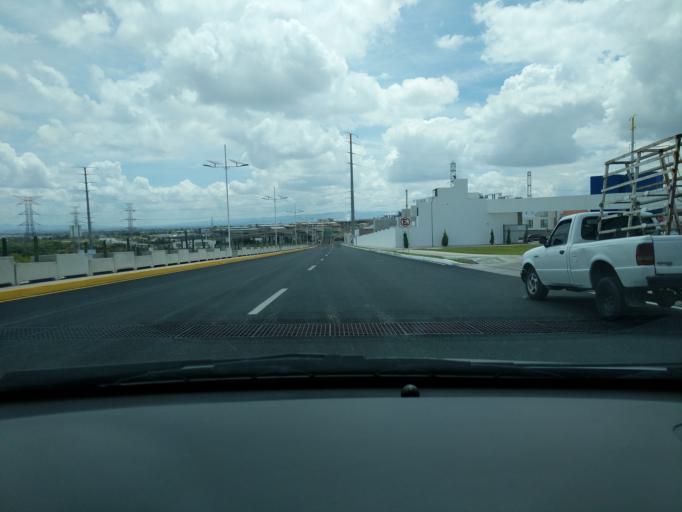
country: MX
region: San Luis Potosi
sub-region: Mexquitic de Carmona
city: Guadalupe Victoria
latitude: 22.1684
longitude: -101.0445
